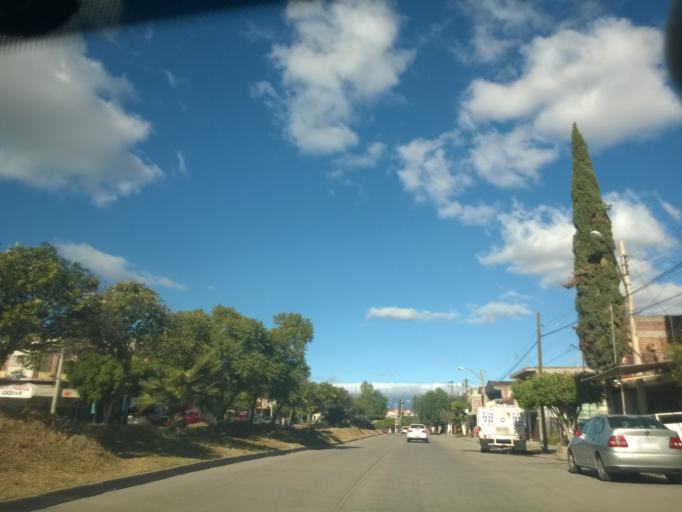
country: MX
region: Guanajuato
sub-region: Leon
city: Ejido la Joya
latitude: 21.1163
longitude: -101.7195
